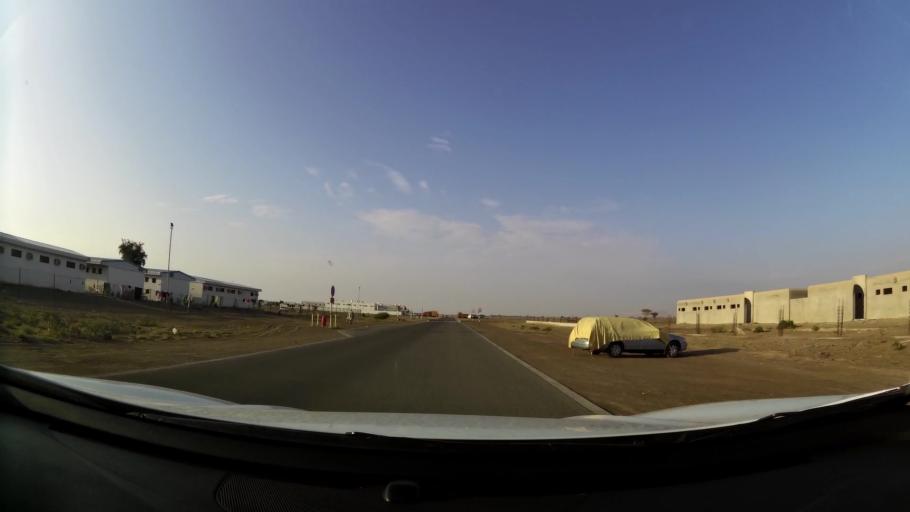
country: AE
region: Abu Dhabi
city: Al Ain
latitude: 24.1443
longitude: 55.8454
